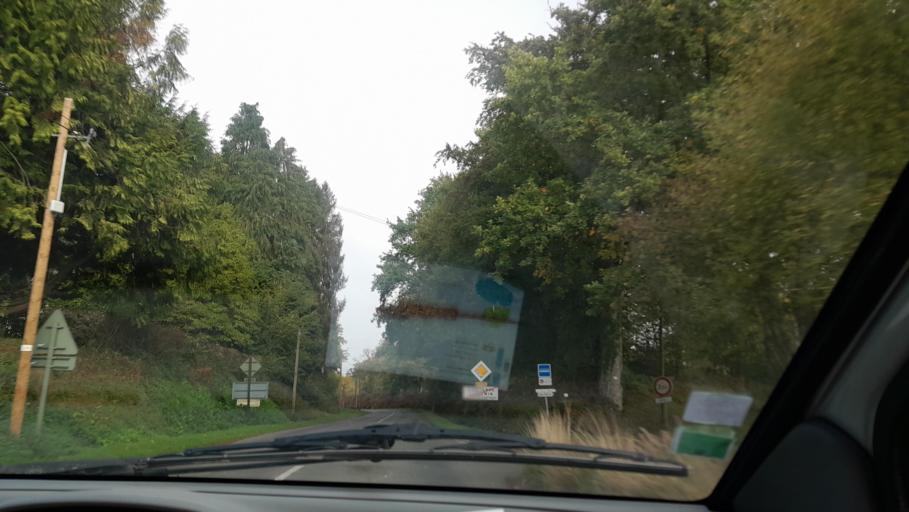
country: FR
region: Brittany
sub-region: Departement d'Ille-et-Vilaine
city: Luitre
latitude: 48.2697
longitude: -1.1472
